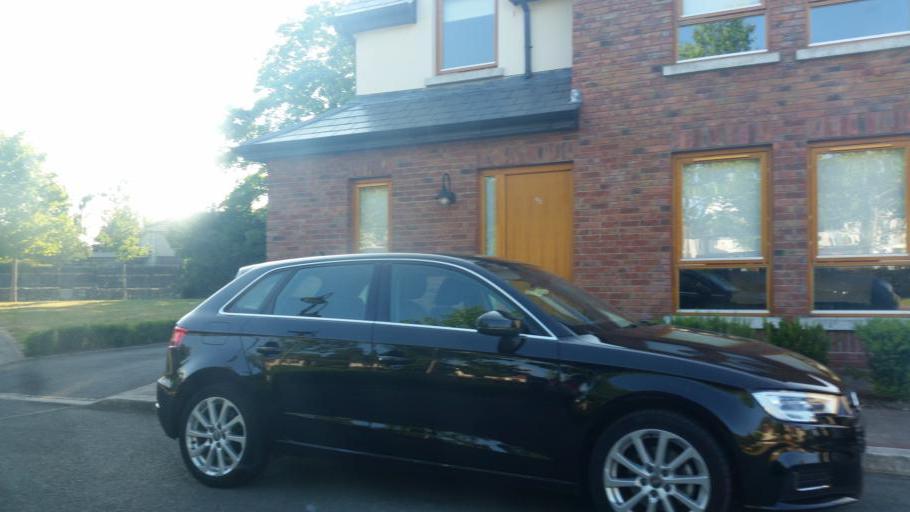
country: IE
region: Leinster
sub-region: Fingal County
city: Blanchardstown
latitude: 53.4340
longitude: -6.3780
